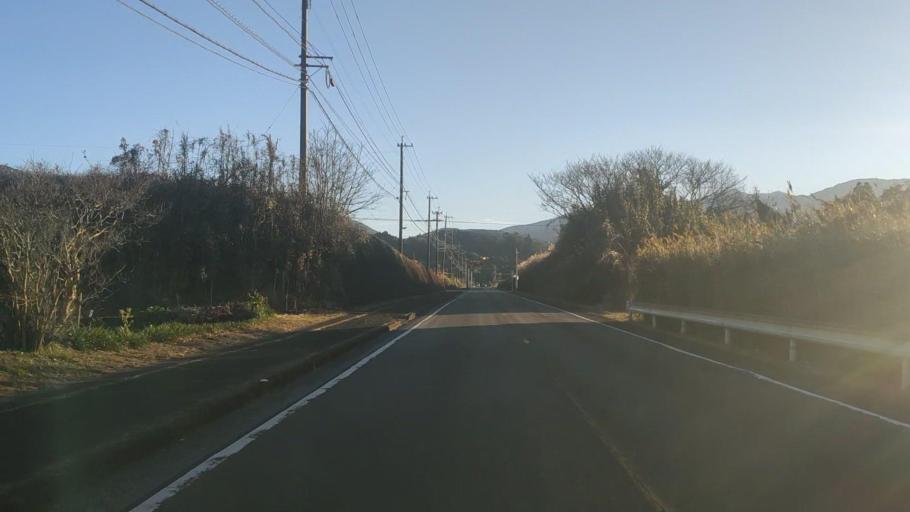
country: JP
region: Miyazaki
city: Miyazaki-shi
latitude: 31.8261
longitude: 131.2985
